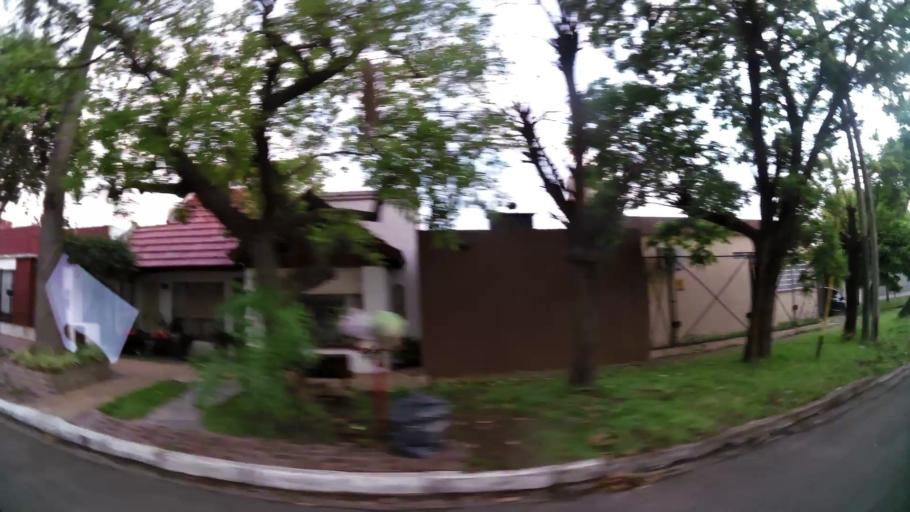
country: AR
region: Buenos Aires
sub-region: Partido de Lomas de Zamora
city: Lomas de Zamora
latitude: -34.7589
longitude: -58.3773
